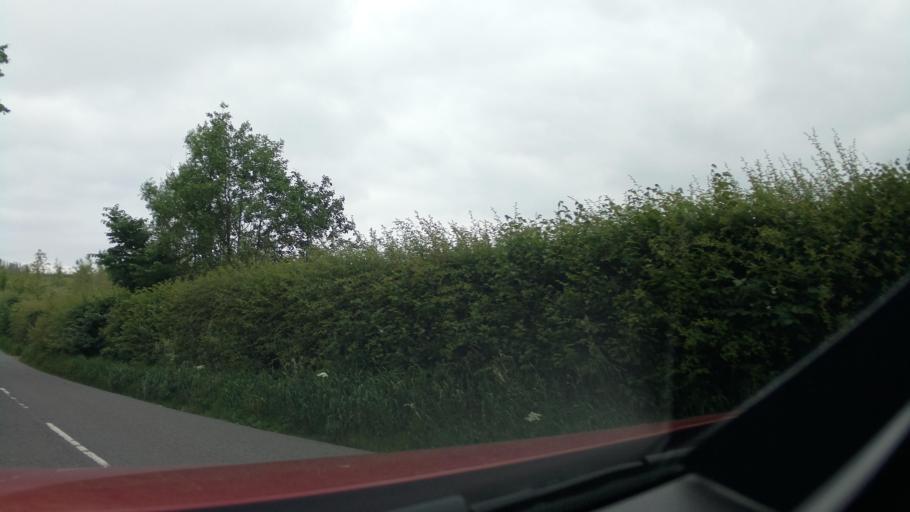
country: GB
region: England
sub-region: District of Rutland
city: Langham
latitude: 52.6801
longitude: -0.8157
